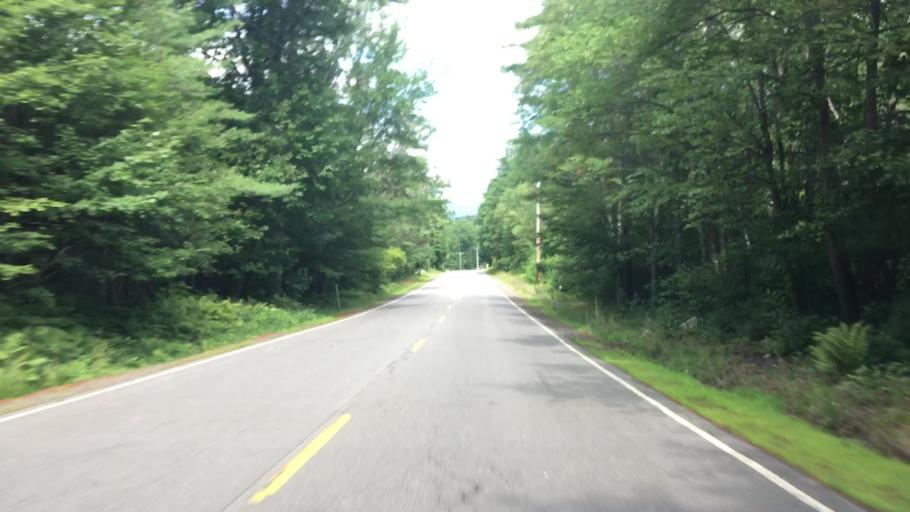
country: US
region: New Hampshire
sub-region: Belknap County
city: Meredith
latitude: 43.6036
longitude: -71.5217
